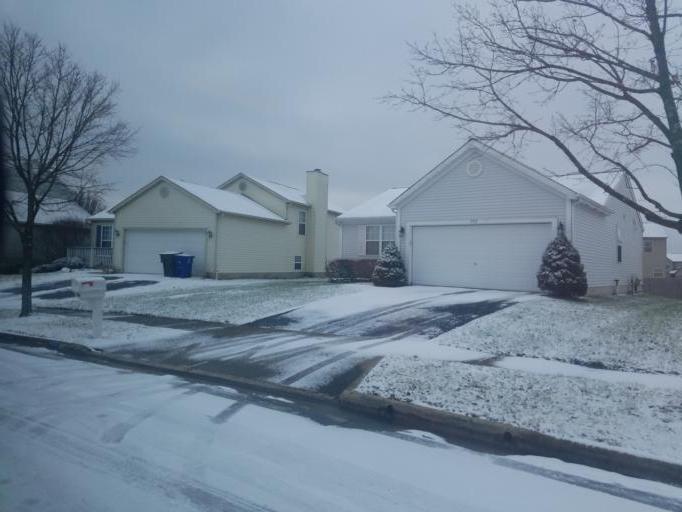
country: US
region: Ohio
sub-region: Franklin County
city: Reynoldsburg
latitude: 39.9949
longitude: -82.7897
